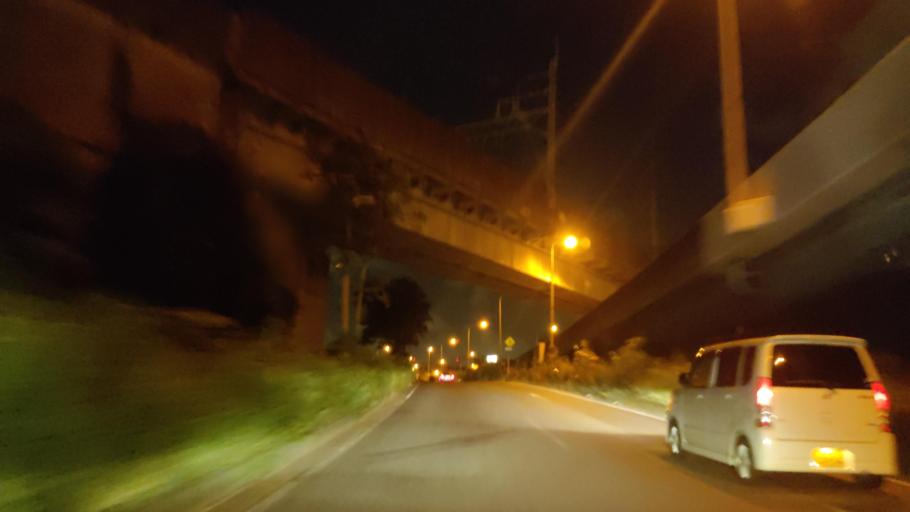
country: JP
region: Chiba
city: Funabashi
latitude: 35.6919
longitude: 139.9592
